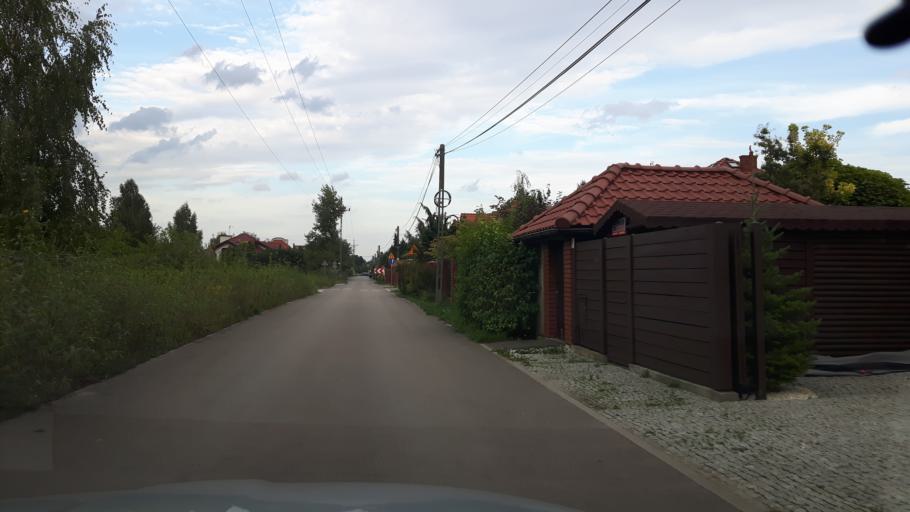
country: PL
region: Masovian Voivodeship
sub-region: Warszawa
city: Targowek
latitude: 52.3099
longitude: 21.0480
